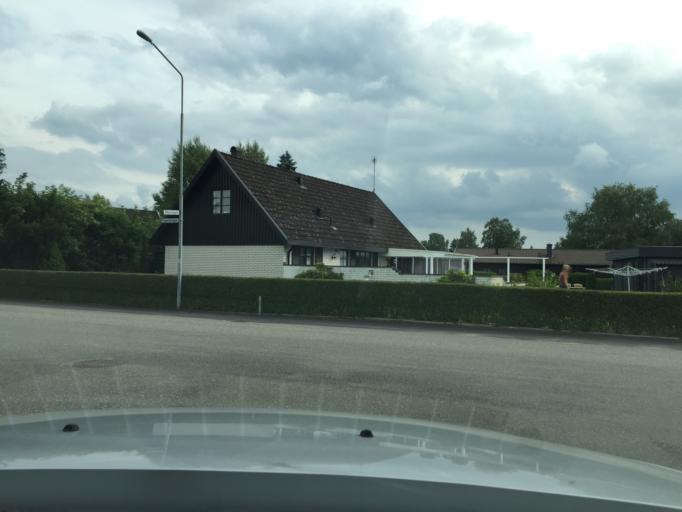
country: SE
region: Skane
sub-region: Hassleholms Kommun
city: Sosdala
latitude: 56.0457
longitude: 13.6781
